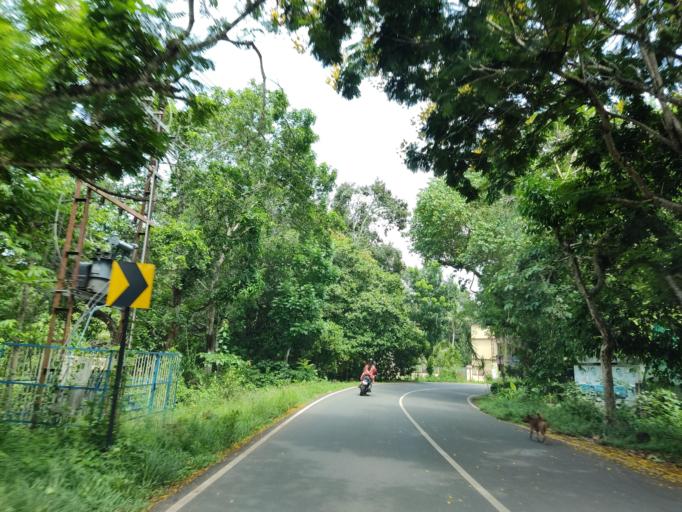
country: IN
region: Kerala
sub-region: Alappuzha
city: Mavelikara
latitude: 9.2707
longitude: 76.5667
